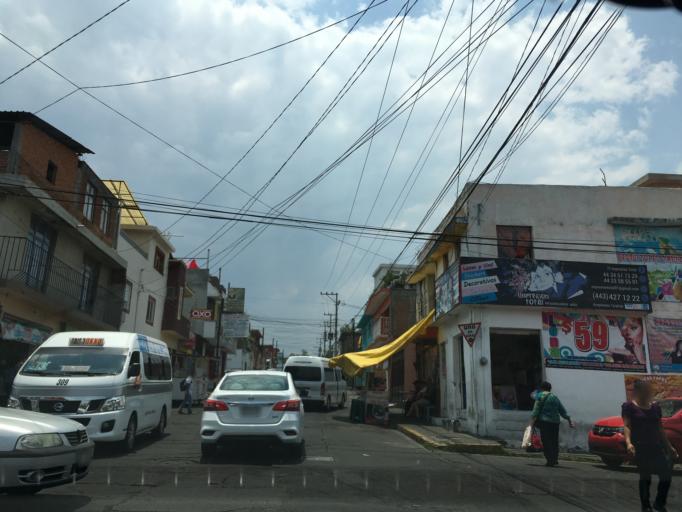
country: MX
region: Michoacan
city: Morelia
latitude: 19.6925
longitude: -101.2033
